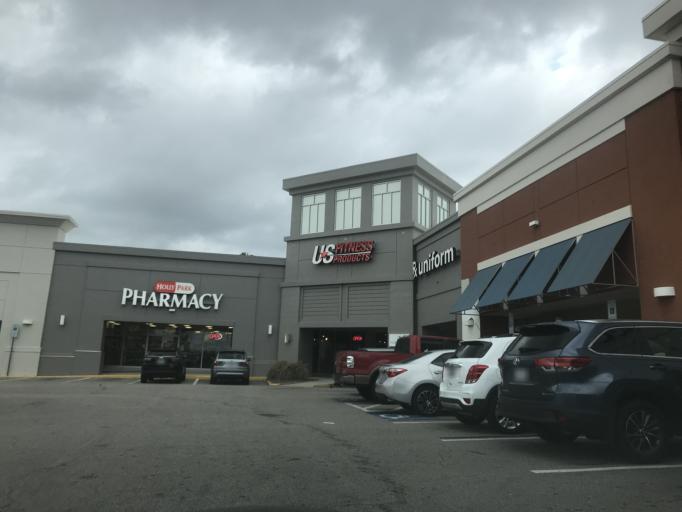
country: US
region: North Carolina
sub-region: Wake County
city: Raleigh
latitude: 35.8230
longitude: -78.6198
